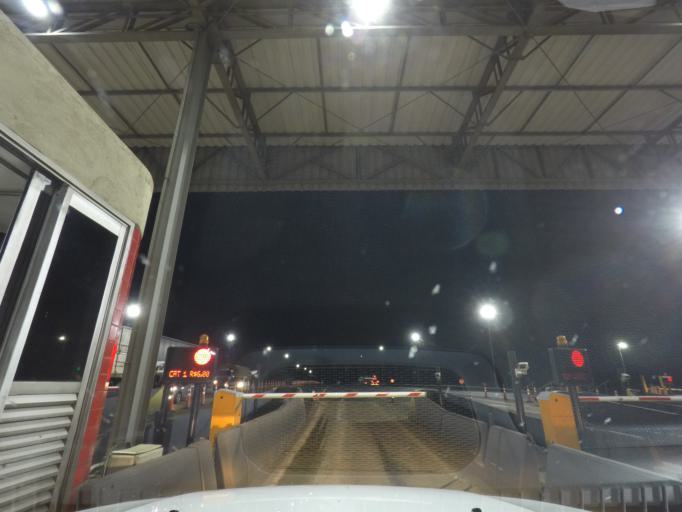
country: BR
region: Minas Gerais
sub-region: Uberlandia
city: Uberlandia
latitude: -19.1808
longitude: -48.1573
